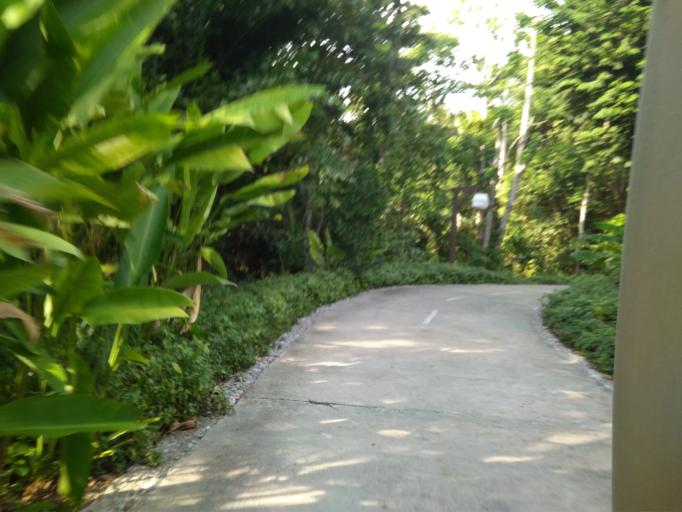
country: TH
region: Krabi
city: Ko Lanta
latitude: 7.4972
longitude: 99.0744
